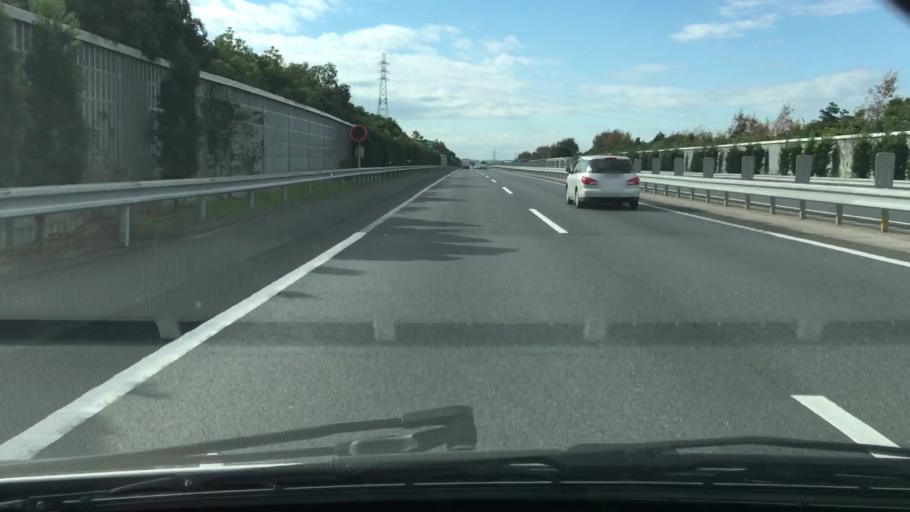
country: JP
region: Chiba
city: Ichihara
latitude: 35.5256
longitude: 140.1267
